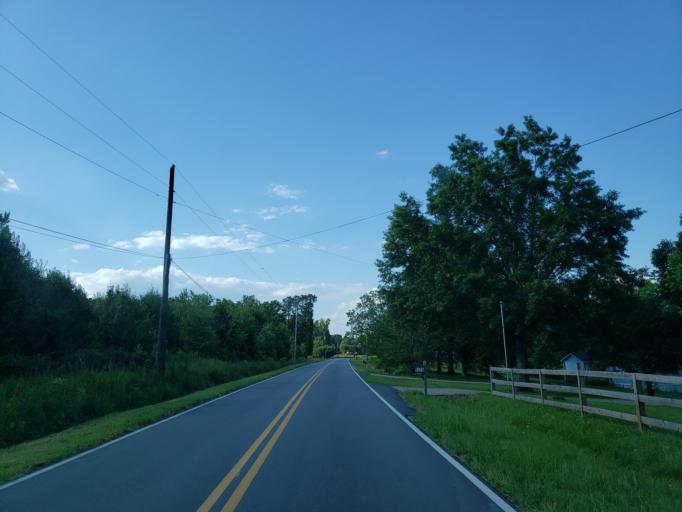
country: US
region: Georgia
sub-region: Haralson County
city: Bremen
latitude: 33.6588
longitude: -85.1134
